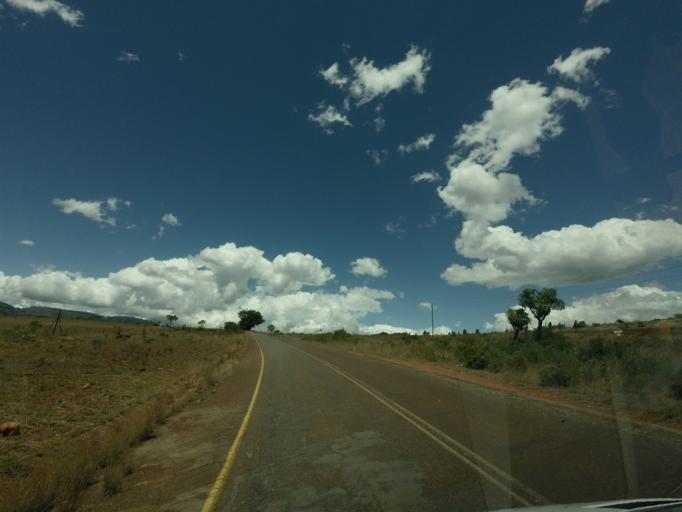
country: ZA
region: Limpopo
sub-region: Mopani District Municipality
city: Hoedspruit
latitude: -24.6085
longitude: 30.7898
